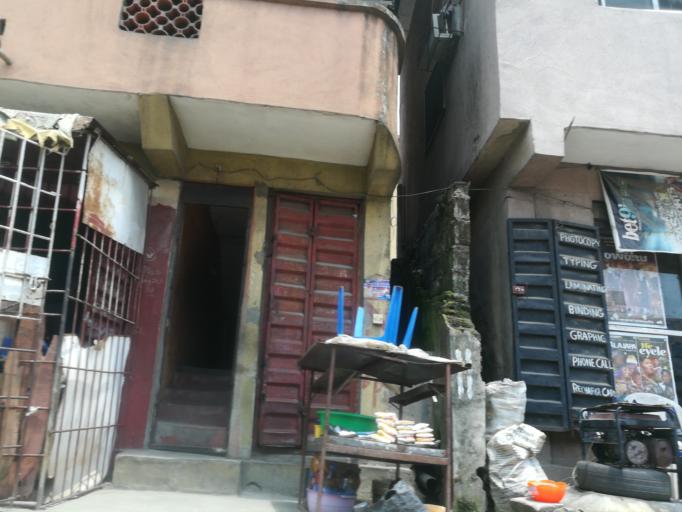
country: NG
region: Lagos
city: Lagos
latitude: 6.4518
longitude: 3.3972
